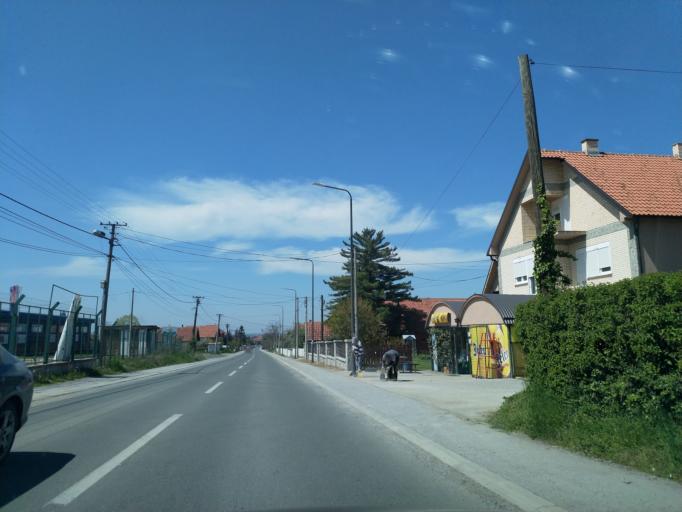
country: RS
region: Central Serbia
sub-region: Belgrade
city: Lazarevac
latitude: 44.3773
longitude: 20.2865
